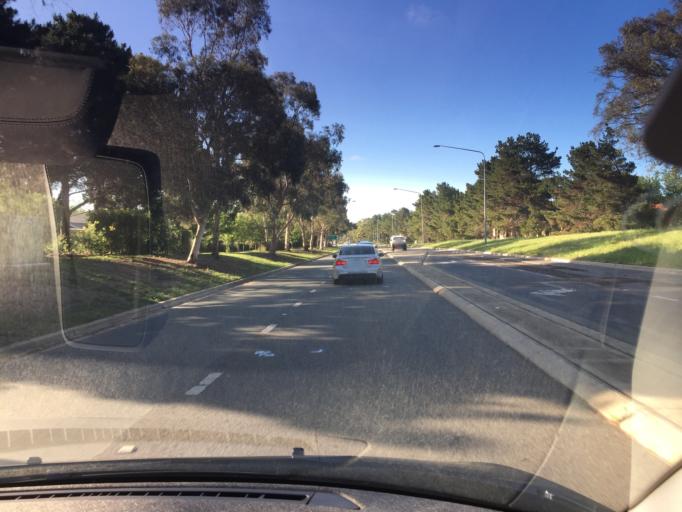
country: AU
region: Australian Capital Territory
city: Kaleen
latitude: -35.2386
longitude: 149.1256
